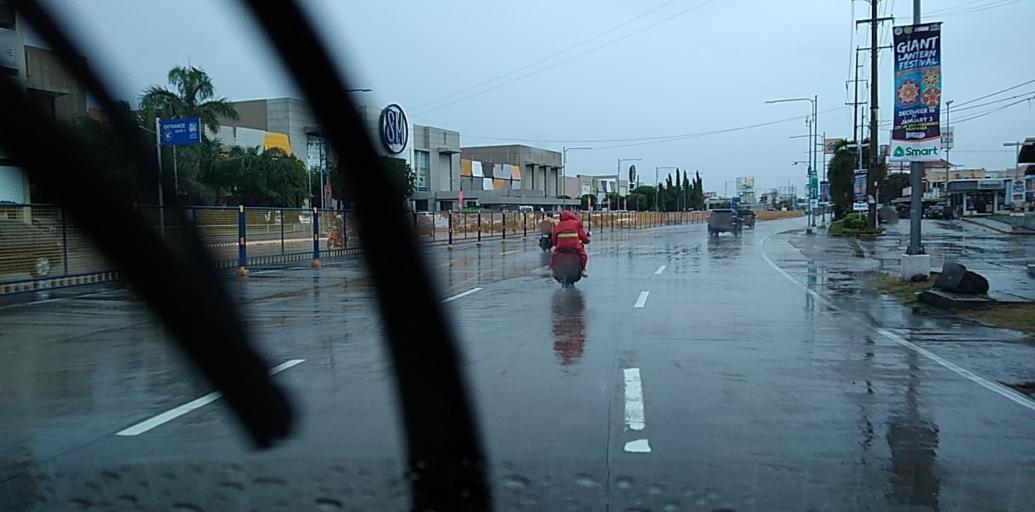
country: PH
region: Central Luzon
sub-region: Province of Pampanga
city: Del Pilar
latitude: 15.0512
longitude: 120.6976
